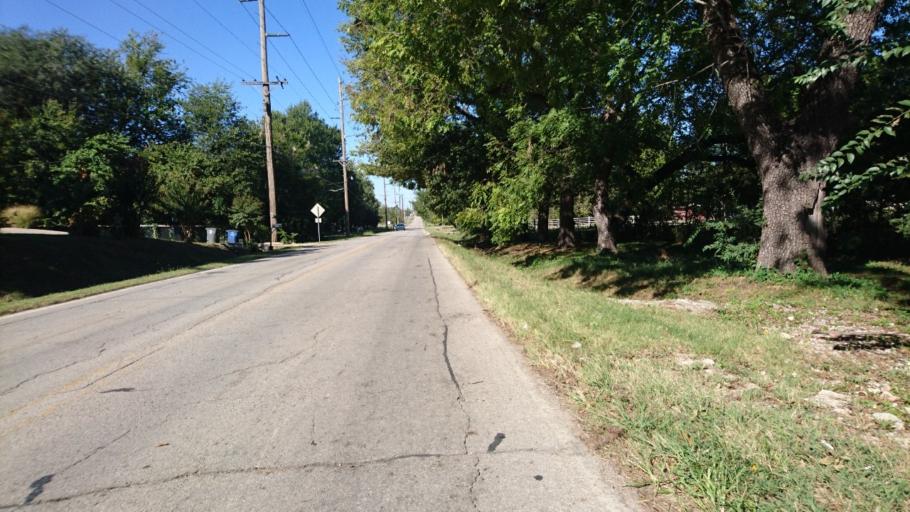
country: US
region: Oklahoma
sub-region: Rogers County
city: Catoosa
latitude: 36.1480
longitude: -95.8166
